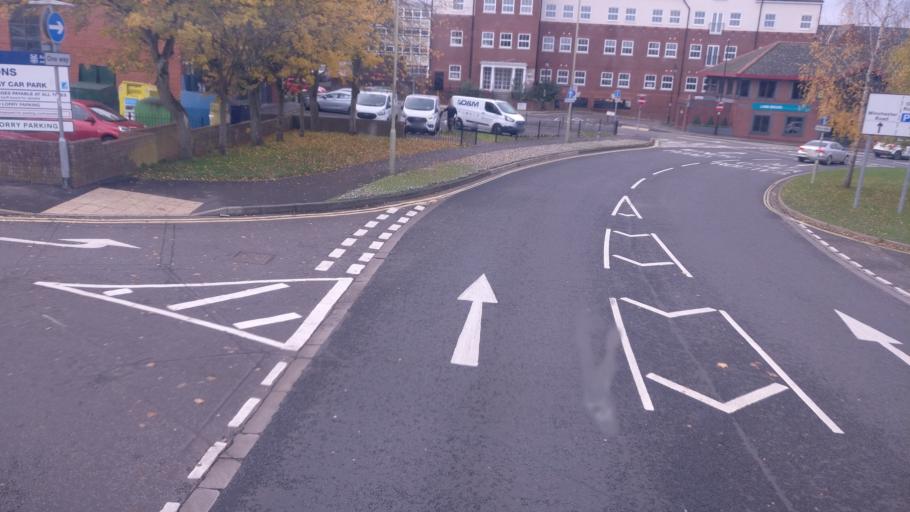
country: GB
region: England
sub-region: Hampshire
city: Basingstoke
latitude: 51.2616
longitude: -1.0878
